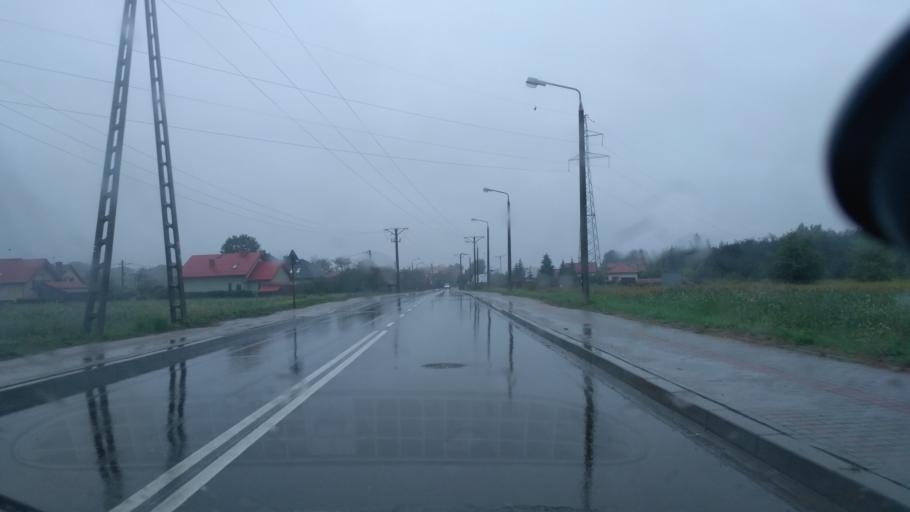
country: PL
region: Subcarpathian Voivodeship
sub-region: Powiat debicki
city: Debica
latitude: 50.0660
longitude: 21.4162
